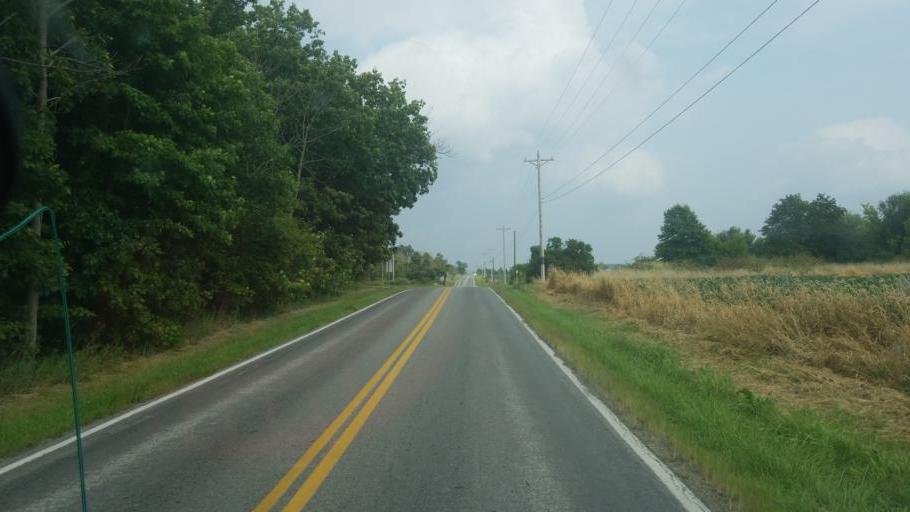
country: US
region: Ohio
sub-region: Wayne County
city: West Salem
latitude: 41.0567
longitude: -82.1709
